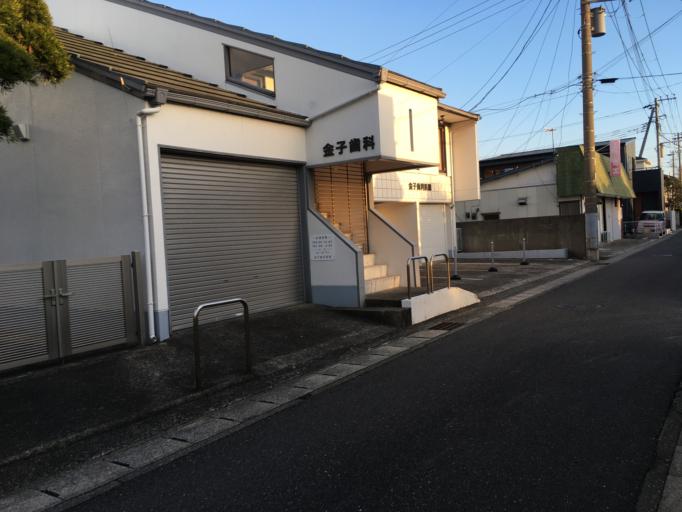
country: JP
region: Chiba
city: Tateyama
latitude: 34.9942
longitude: 139.8661
